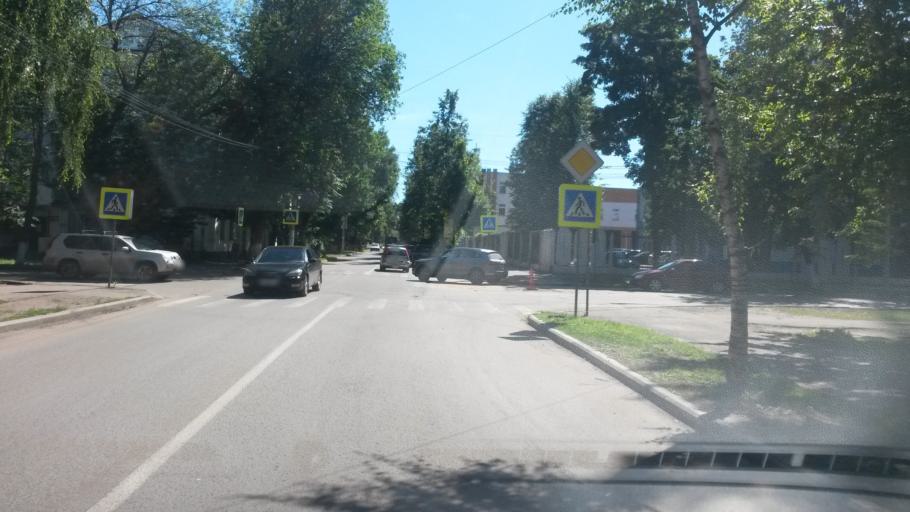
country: RU
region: Jaroslavl
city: Yaroslavl
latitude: 57.6310
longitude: 39.8639
